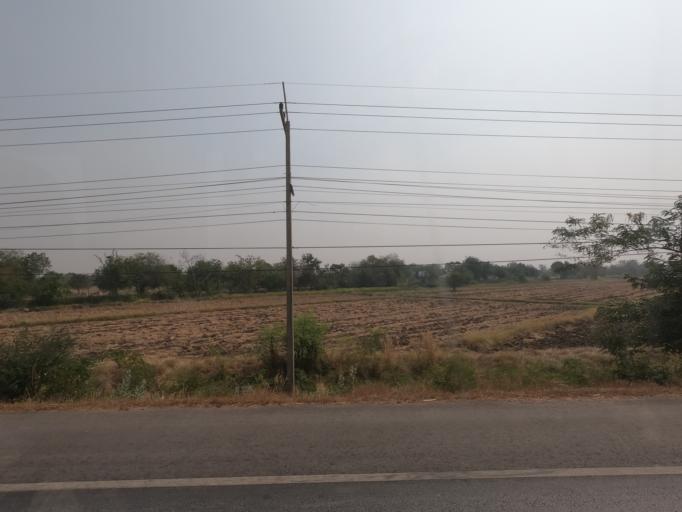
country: TH
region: Nakhon Ratchasima
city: Phimai
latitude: 15.3352
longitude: 102.4405
